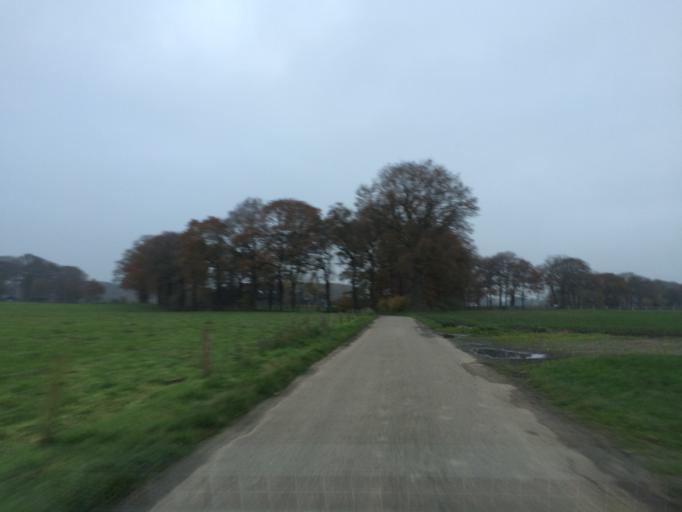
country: DE
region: North Rhine-Westphalia
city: Marl
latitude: 51.6834
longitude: 7.0313
